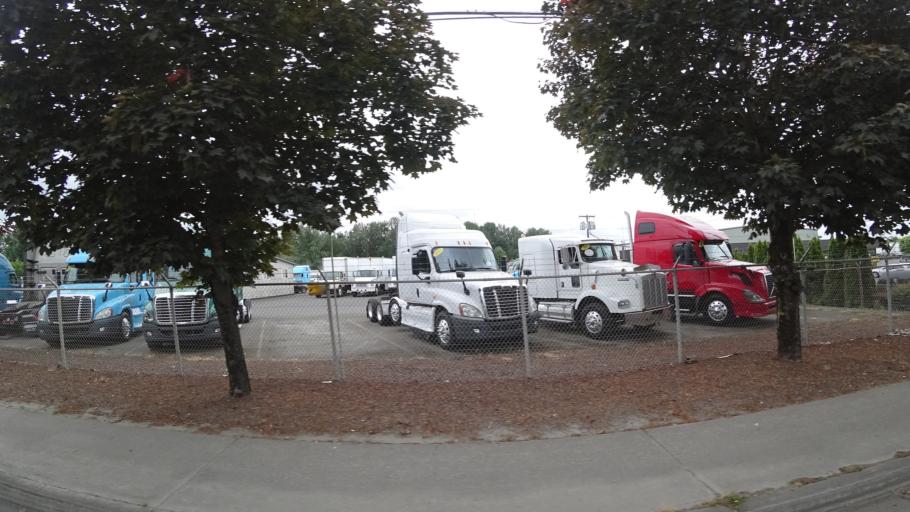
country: US
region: Washington
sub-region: Clark County
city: Vancouver
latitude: 45.5913
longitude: -122.6627
